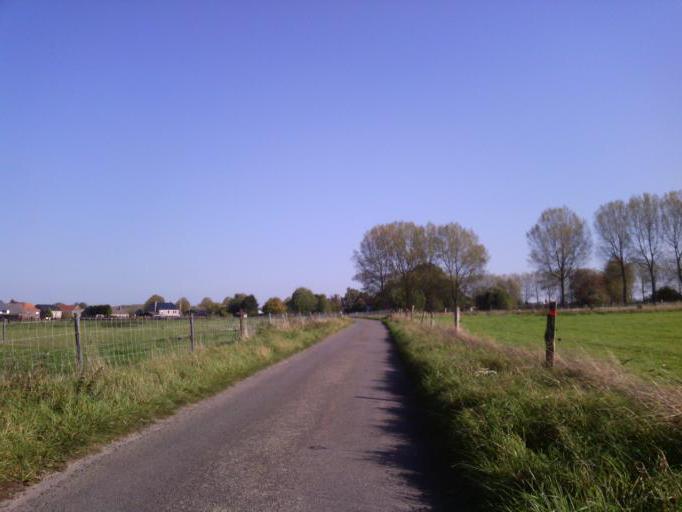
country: BE
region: Wallonia
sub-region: Province du Hainaut
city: Beloeil
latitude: 50.5600
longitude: 3.6781
